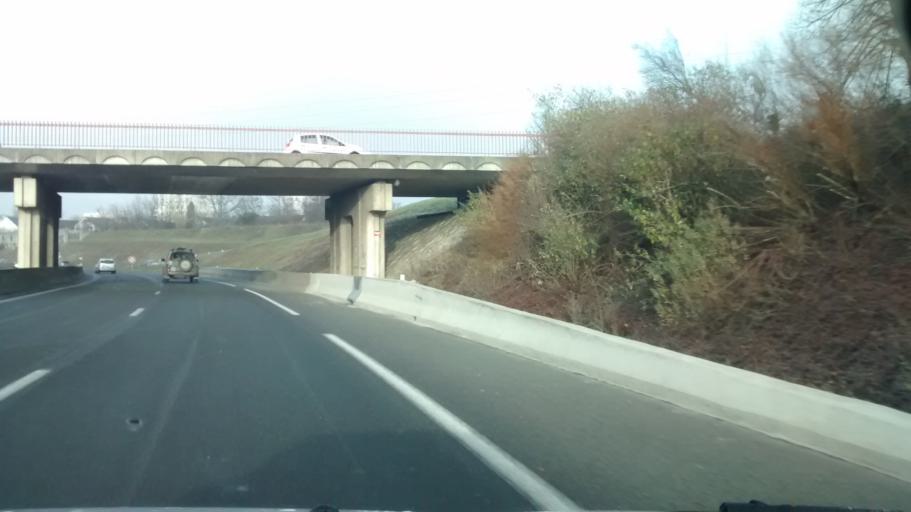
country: FR
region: Centre
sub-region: Departement d'Indre-et-Loire
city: Joue-les-Tours
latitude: 47.3394
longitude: 0.6675
